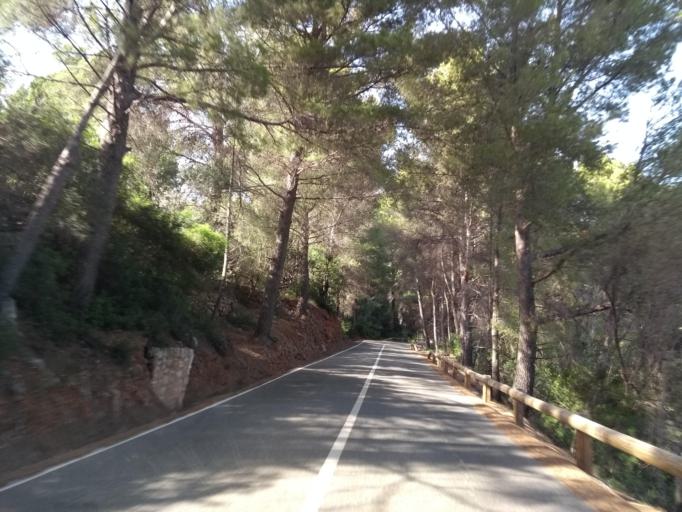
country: ES
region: Balearic Islands
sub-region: Illes Balears
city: Soller
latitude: 39.7794
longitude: 2.7232
